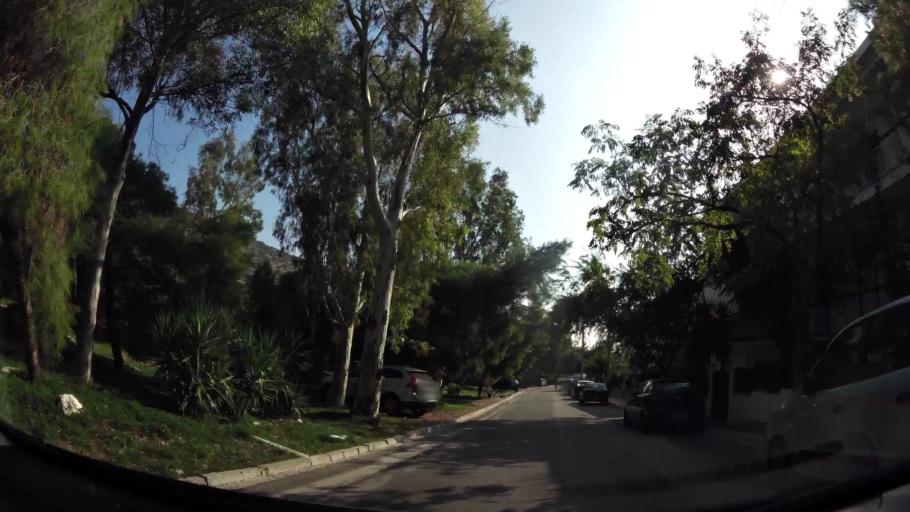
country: GR
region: Attica
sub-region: Nomarchia Athinas
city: Argyroupoli
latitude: 37.9089
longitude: 23.7591
